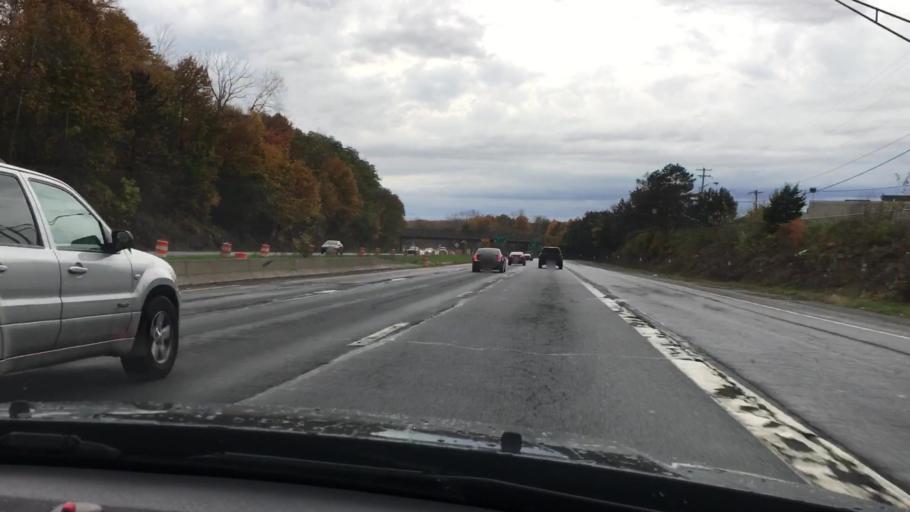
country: US
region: New York
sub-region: Orange County
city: Balmville
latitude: 41.5197
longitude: -74.0269
